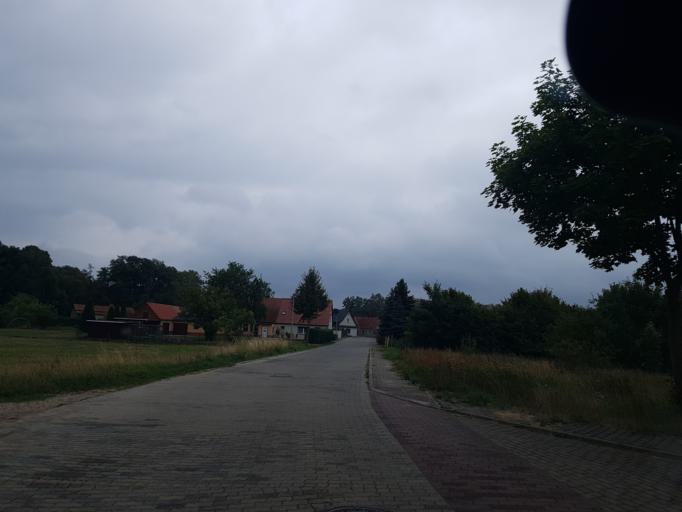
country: DE
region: Saxony-Anhalt
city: Loburg
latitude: 52.2431
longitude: 12.0477
